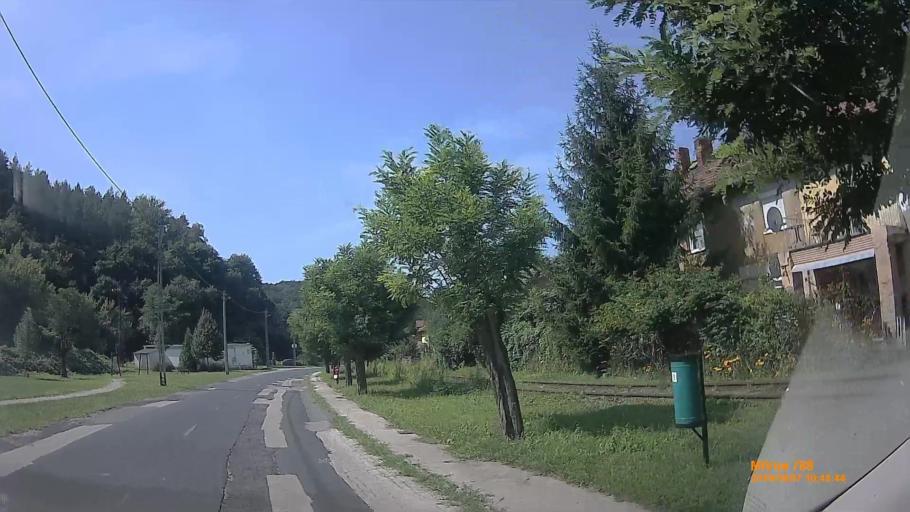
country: HU
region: Veszprem
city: Ajka
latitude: 47.0881
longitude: 17.5824
